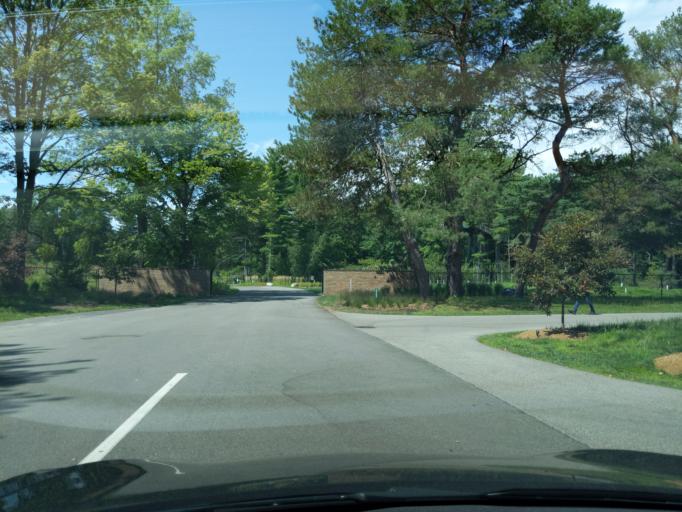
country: US
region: Michigan
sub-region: Midland County
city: Midland
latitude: 43.6285
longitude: -84.2474
